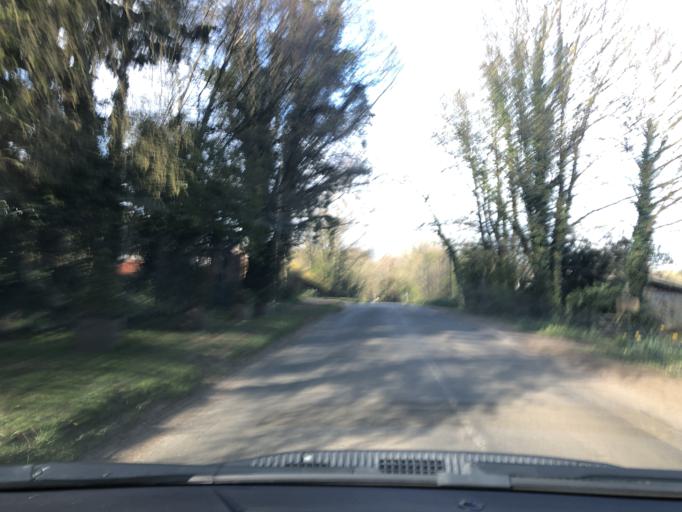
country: GB
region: England
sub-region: Oxfordshire
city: Bloxham
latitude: 52.0302
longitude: -1.4149
